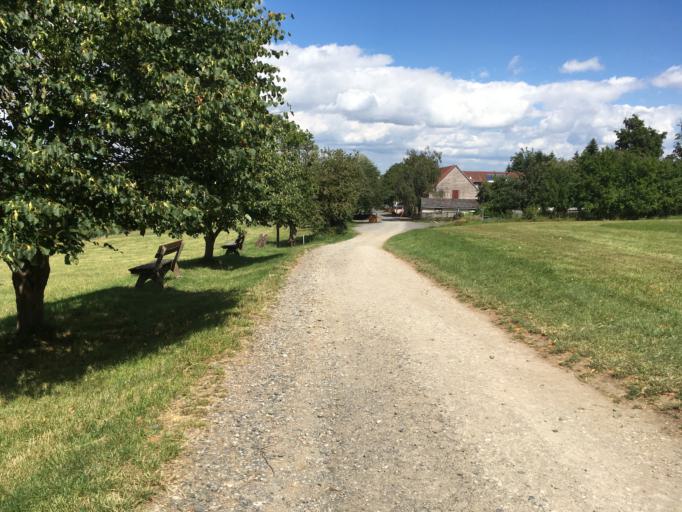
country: DE
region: Hesse
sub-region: Regierungsbezirk Kassel
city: Zierenberg
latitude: 51.3527
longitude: 9.3369
